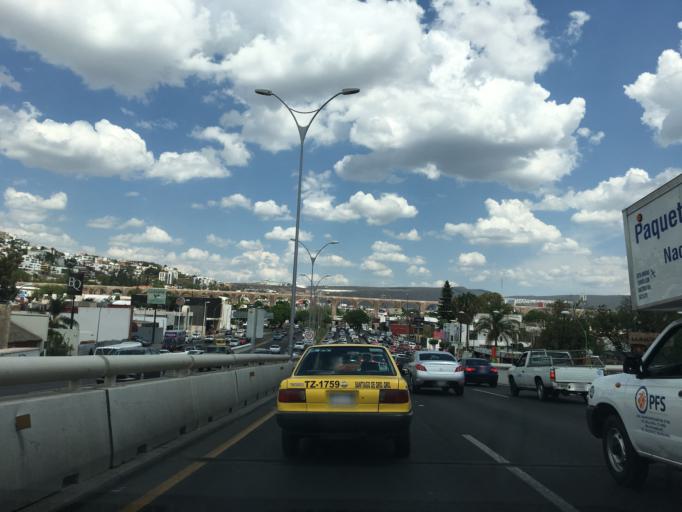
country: MX
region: Queretaro
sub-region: Queretaro
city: Santiago de Queretaro
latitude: 20.5996
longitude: -100.3754
